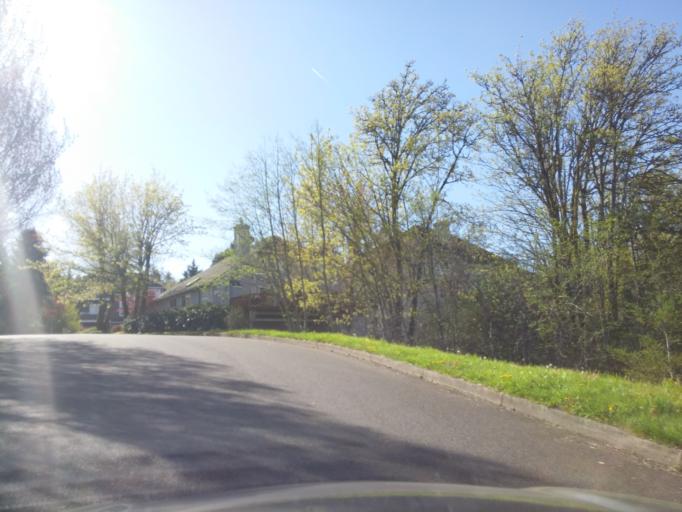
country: US
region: Oregon
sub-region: Washington County
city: West Haven
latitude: 45.5357
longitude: -122.7838
